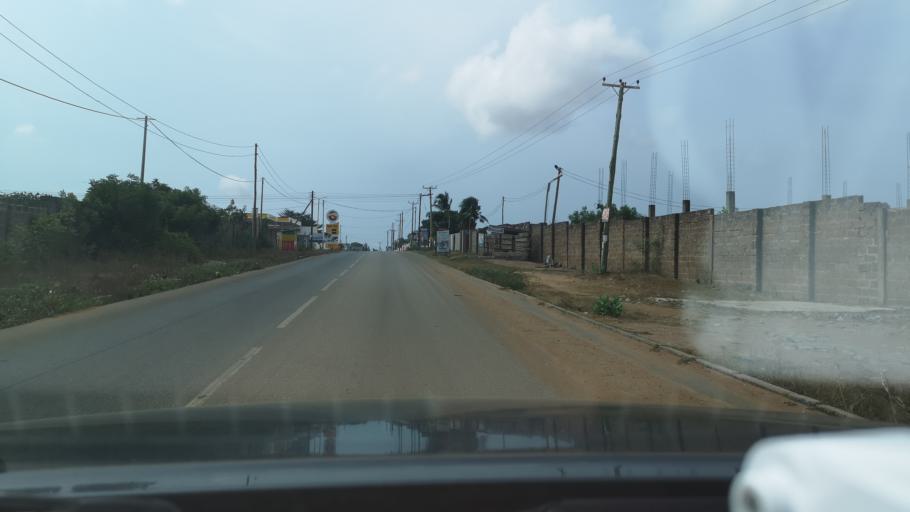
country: GH
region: Greater Accra
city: Tema
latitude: 5.6783
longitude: -0.0311
